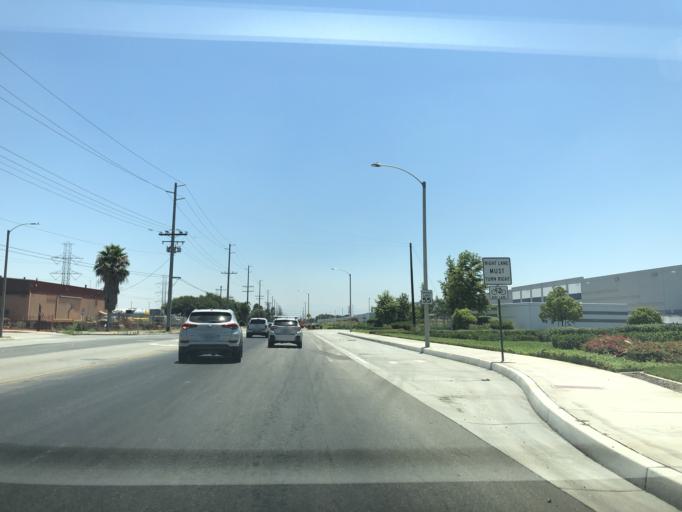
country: US
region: California
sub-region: San Bernardino County
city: Rancho Cucamonga
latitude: 34.0988
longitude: -117.5239
